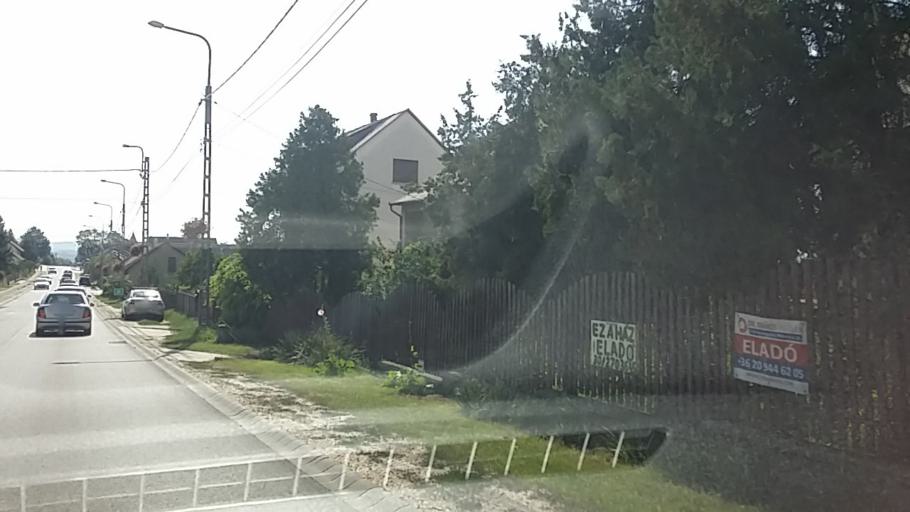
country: HU
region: Pest
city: Erdokertes
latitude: 47.6715
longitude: 19.3098
